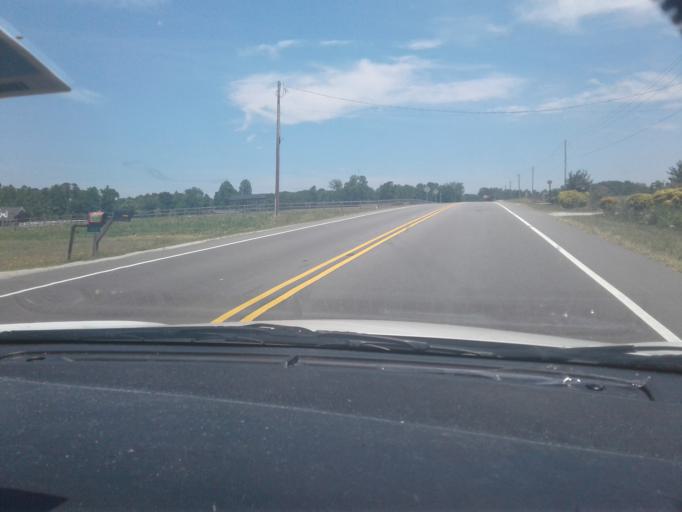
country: US
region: North Carolina
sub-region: Harnett County
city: Lillington
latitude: 35.4496
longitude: -78.8286
